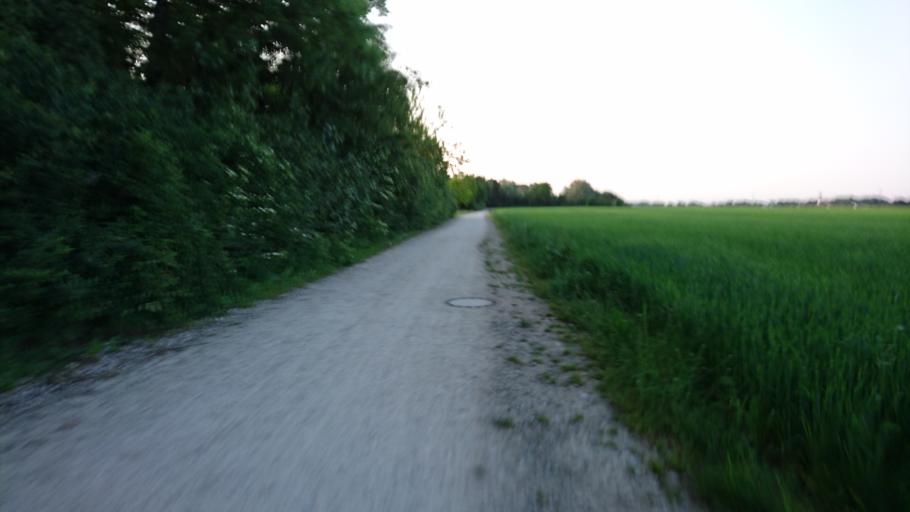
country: DE
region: Bavaria
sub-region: Upper Bavaria
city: Pliening
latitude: 48.1838
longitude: 11.8033
